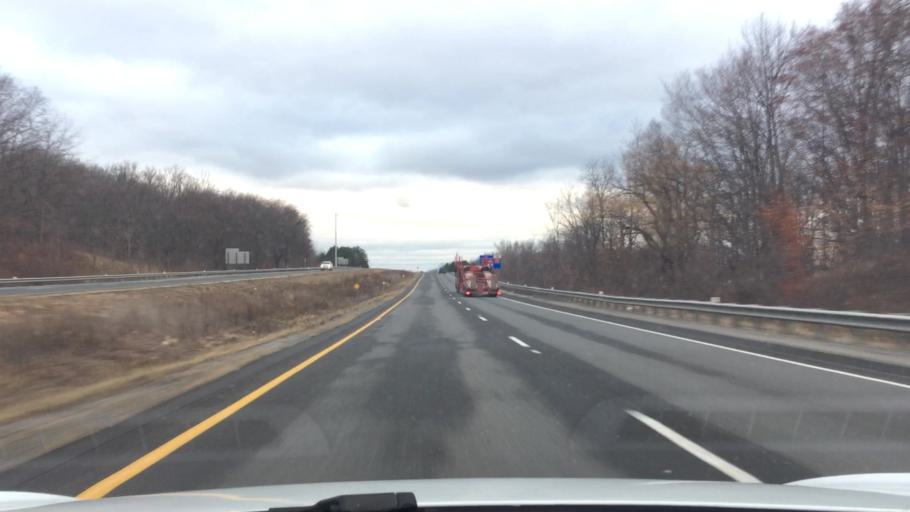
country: CA
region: Ontario
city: Niagara Falls
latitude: 43.1512
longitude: -79.1183
